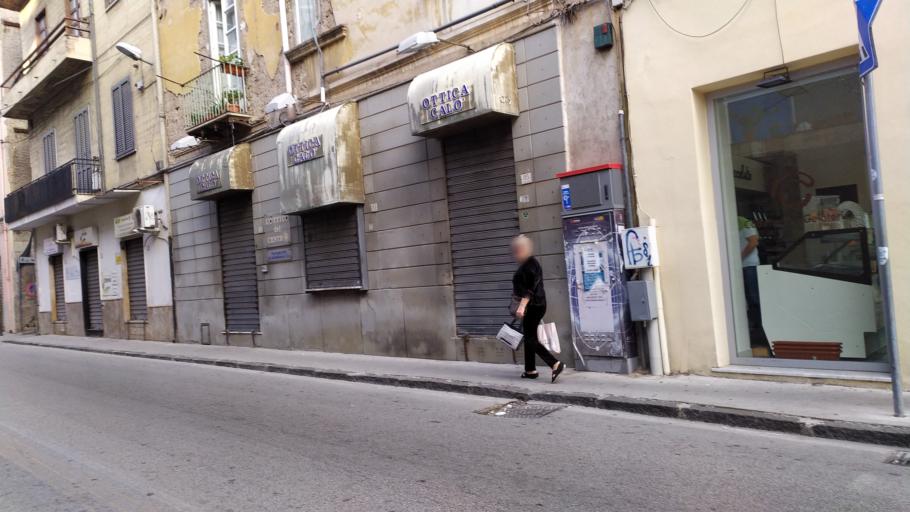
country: IT
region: Campania
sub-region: Provincia di Caserta
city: San Nicola la Strada
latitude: 41.0688
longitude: 14.3331
